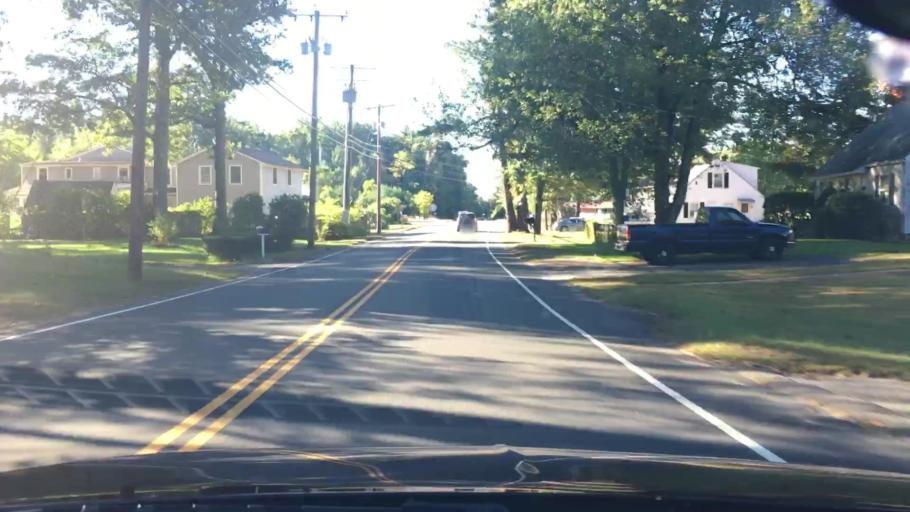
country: US
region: Connecticut
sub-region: Hartford County
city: Sherwood Manor
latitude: 42.0246
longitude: -72.5597
